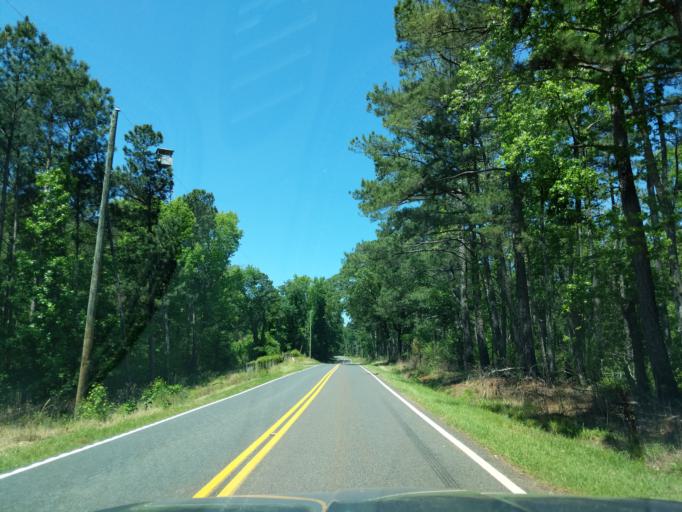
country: US
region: Georgia
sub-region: Columbia County
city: Evans
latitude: 33.6241
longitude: -82.1261
